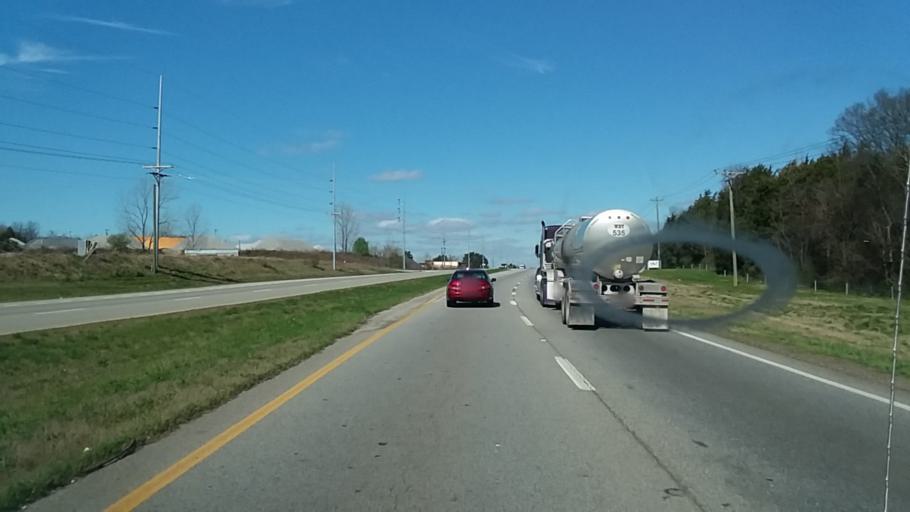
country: US
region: Alabama
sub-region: Morgan County
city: Trinity
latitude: 34.6209
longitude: -87.0769
